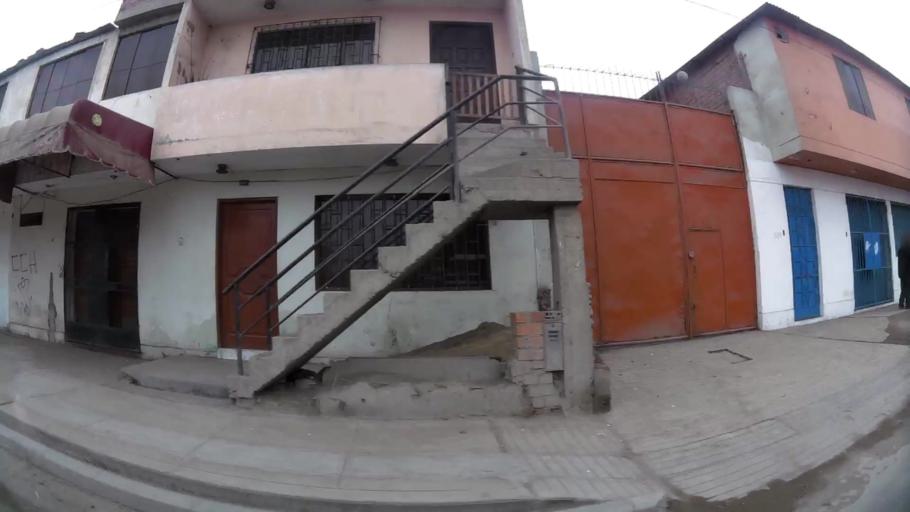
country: PE
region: Lima
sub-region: Lima
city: Cieneguilla
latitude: -12.2228
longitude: -76.9081
